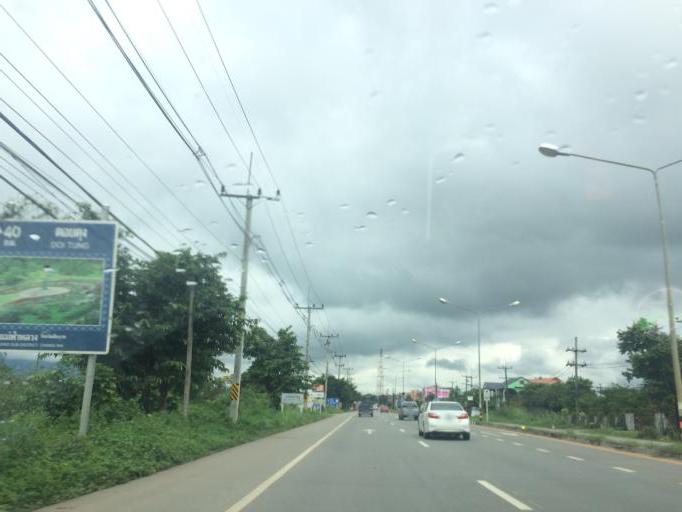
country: TH
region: Chiang Rai
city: Mae Chan
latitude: 20.0392
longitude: 99.8756
